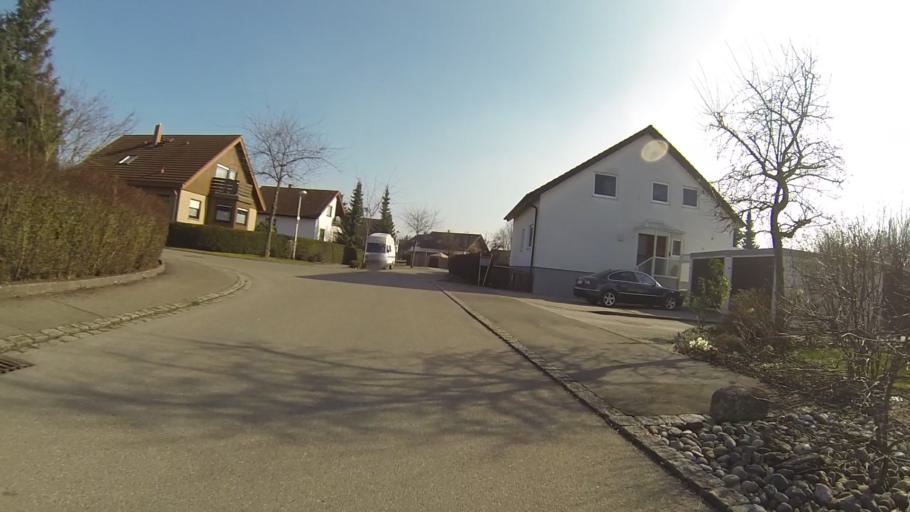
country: DE
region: Baden-Wuerttemberg
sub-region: Regierungsbezirk Stuttgart
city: Bolheim
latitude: 48.6328
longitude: 10.1558
